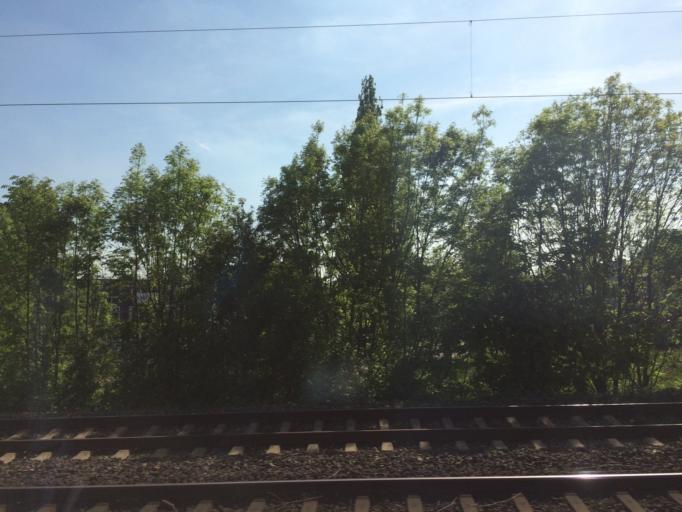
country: DE
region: North Rhine-Westphalia
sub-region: Regierungsbezirk Dusseldorf
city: Muelheim (Ruhr)
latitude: 51.4326
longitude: 6.8820
